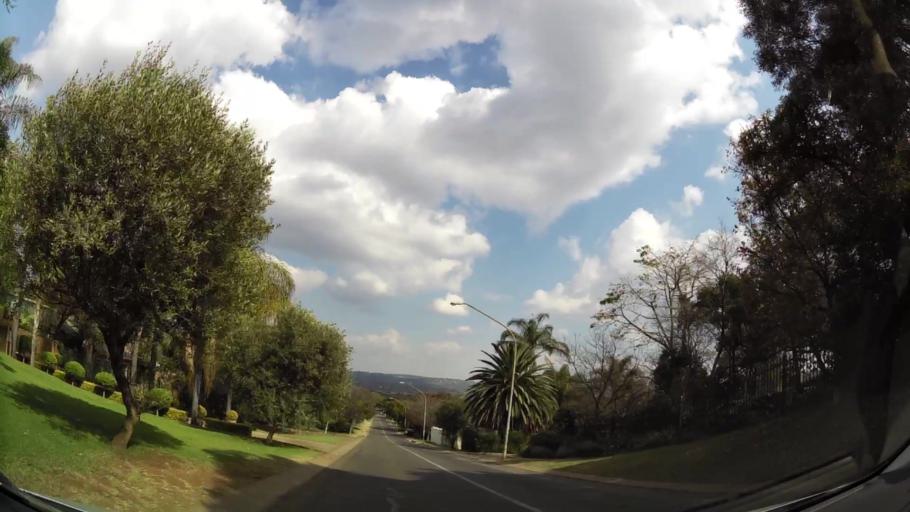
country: ZA
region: Gauteng
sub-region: City of Tshwane Metropolitan Municipality
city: Pretoria
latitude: -25.7779
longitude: 28.3138
